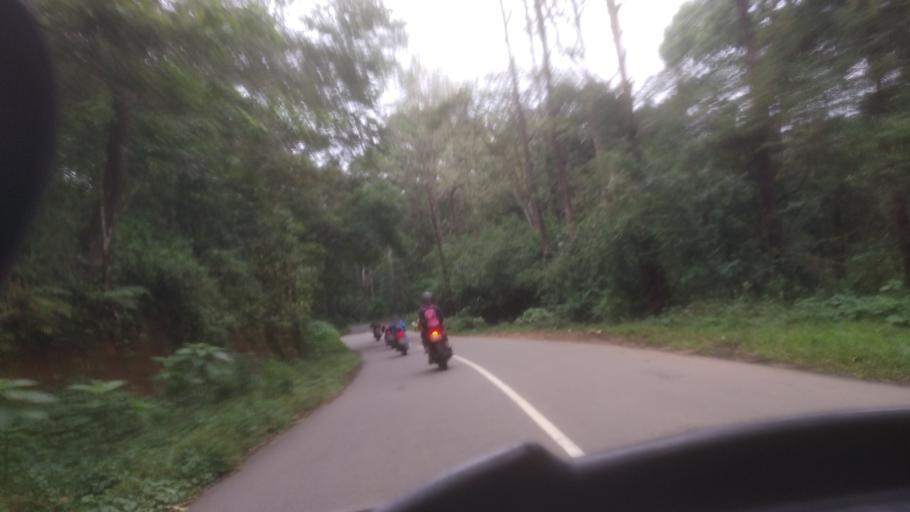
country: IN
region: Tamil Nadu
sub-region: Theni
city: Kombai
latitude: 9.8935
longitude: 77.1569
